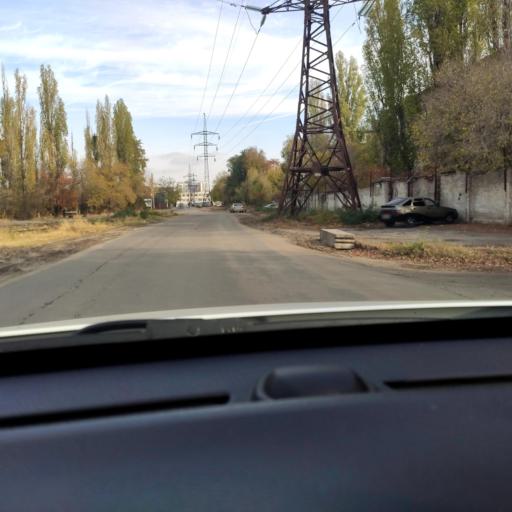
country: RU
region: Voronezj
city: Voronezh
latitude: 51.6391
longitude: 39.1540
